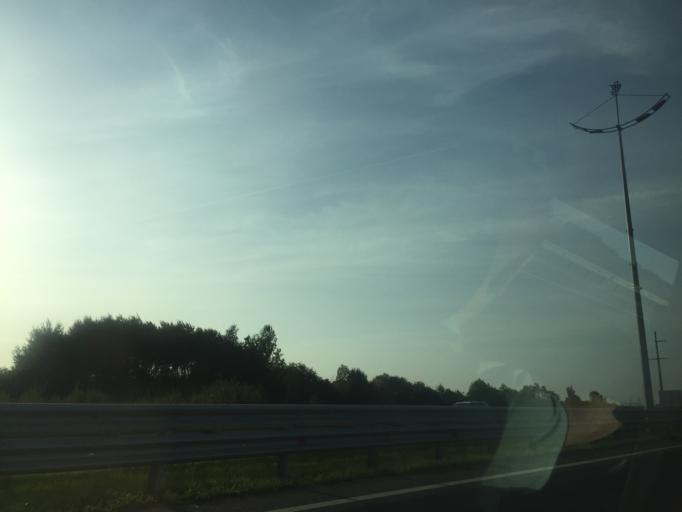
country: RU
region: Kaliningrad
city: Maloye Isakovo
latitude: 54.7561
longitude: 20.5828
